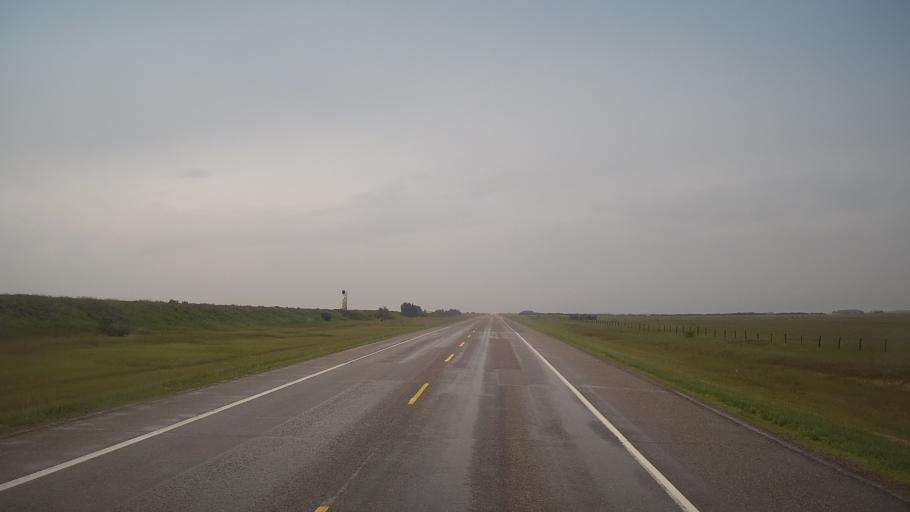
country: CA
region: Saskatchewan
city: Wilkie
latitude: 52.2169
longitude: -108.5062
